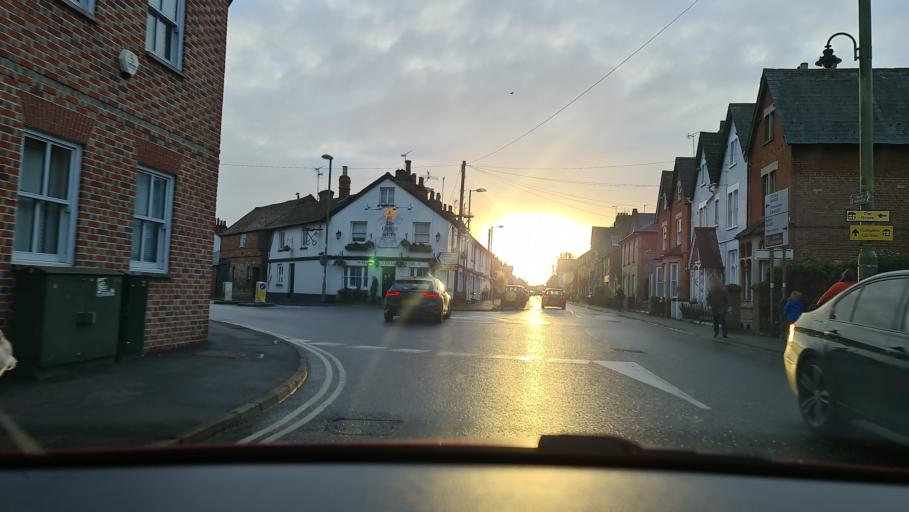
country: GB
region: England
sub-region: Oxfordshire
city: Thame
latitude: 51.7453
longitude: -0.9740
